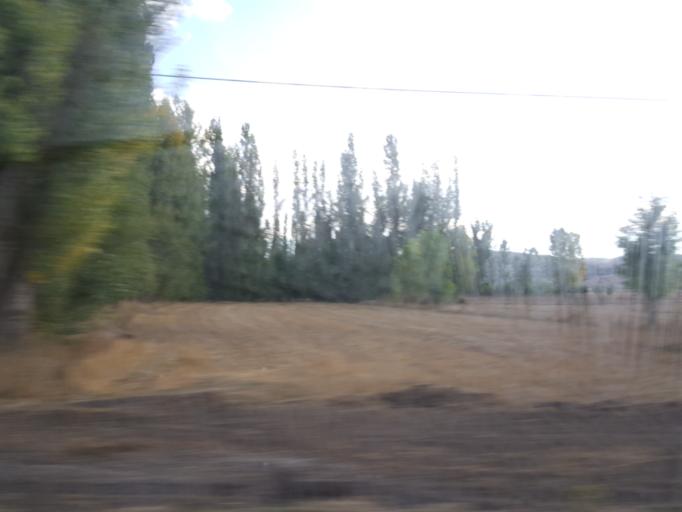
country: TR
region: Tokat
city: Yesilyurt
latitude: 40.0252
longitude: 36.2903
